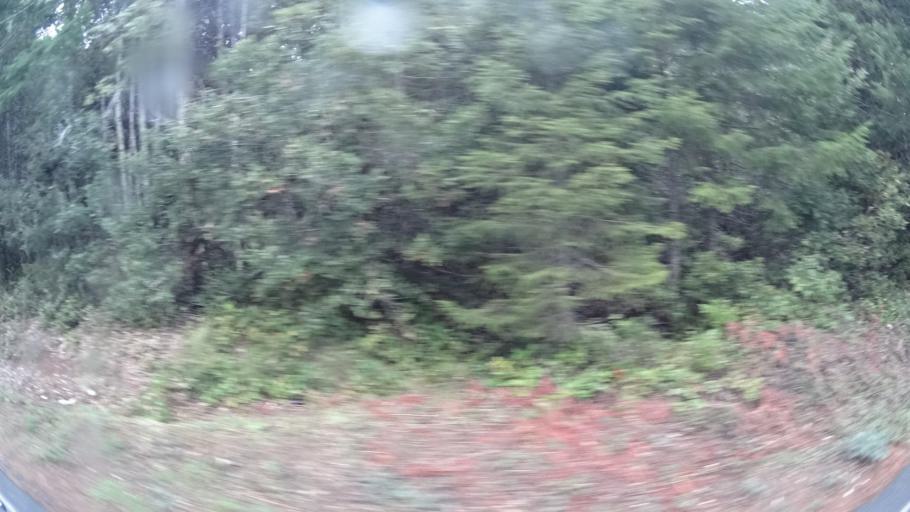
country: US
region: California
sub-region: Humboldt County
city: Willow Creek
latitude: 41.1837
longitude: -123.8149
